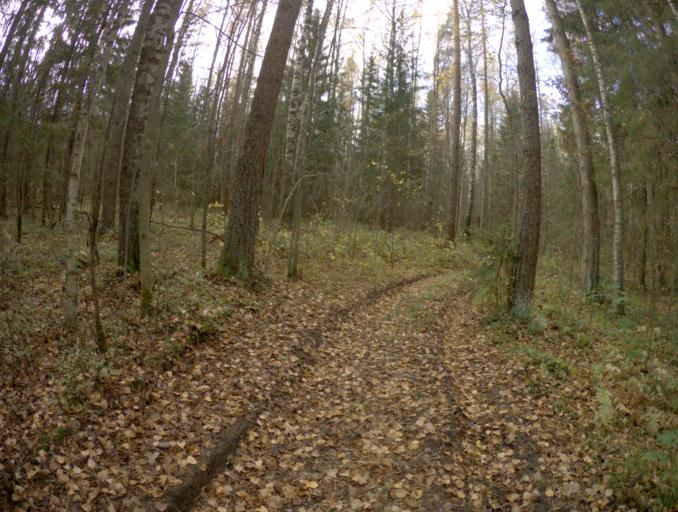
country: RU
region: Vladimir
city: Raduzhnyy
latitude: 55.9647
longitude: 40.3584
